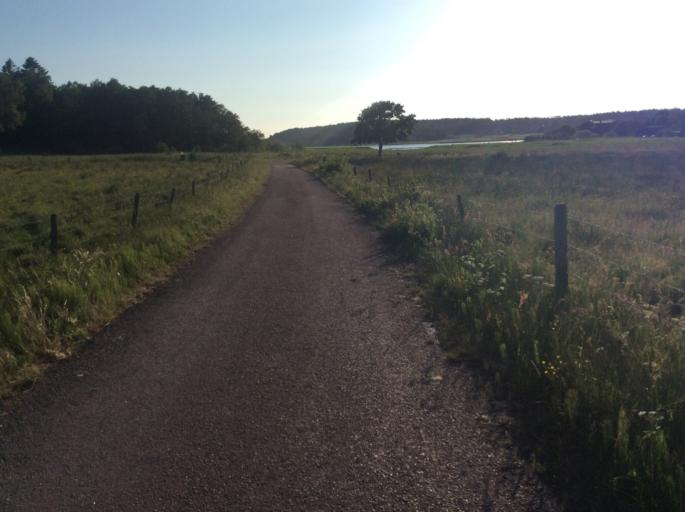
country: SE
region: Vaestra Goetaland
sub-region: Goteborg
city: Torslanda
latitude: 57.7973
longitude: 11.8583
